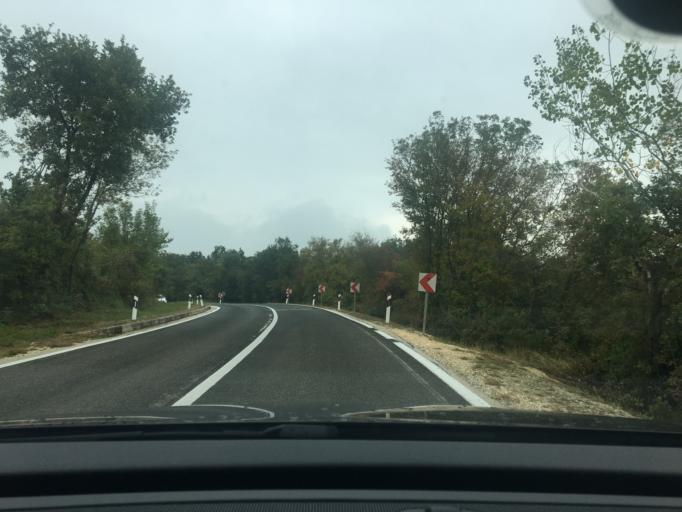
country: HR
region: Istarska
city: Buje
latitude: 45.4328
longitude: 13.6581
